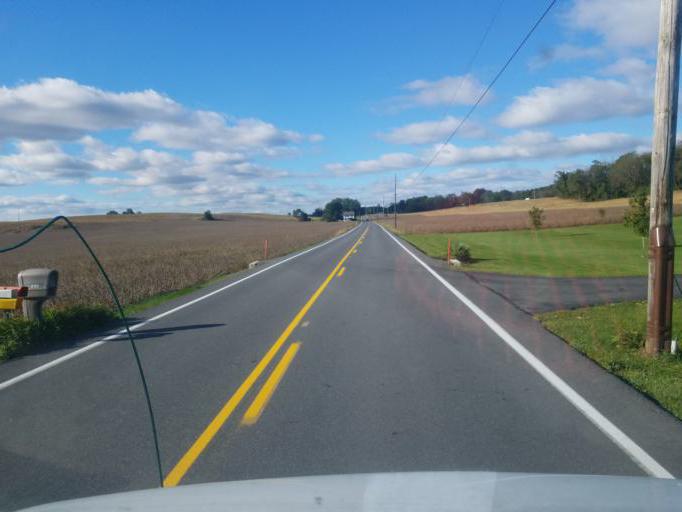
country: US
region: Pennsylvania
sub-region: Franklin County
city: Guilford Siding
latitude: 39.8464
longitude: -77.6140
